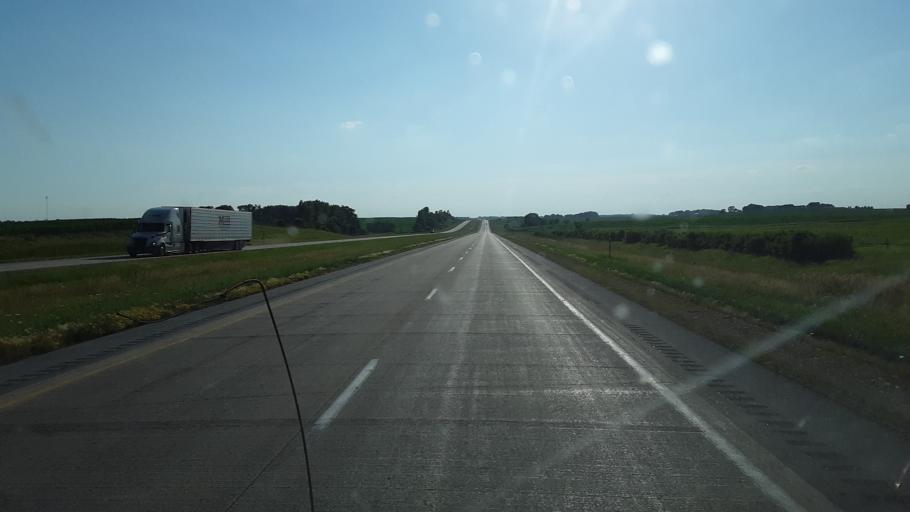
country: US
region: Iowa
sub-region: Hardin County
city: Iowa Falls
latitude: 42.4483
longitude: -93.3018
